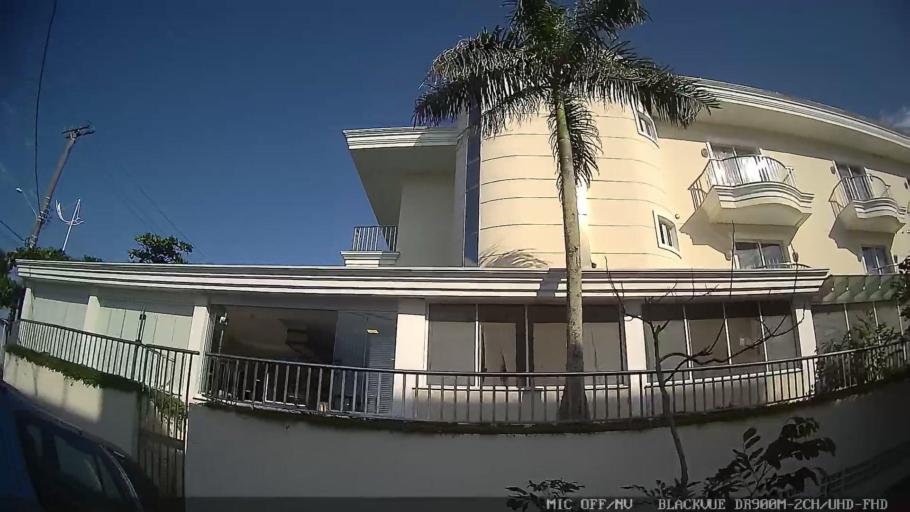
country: BR
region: Sao Paulo
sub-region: Guaruja
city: Guaruja
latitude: -23.9854
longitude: -46.2214
